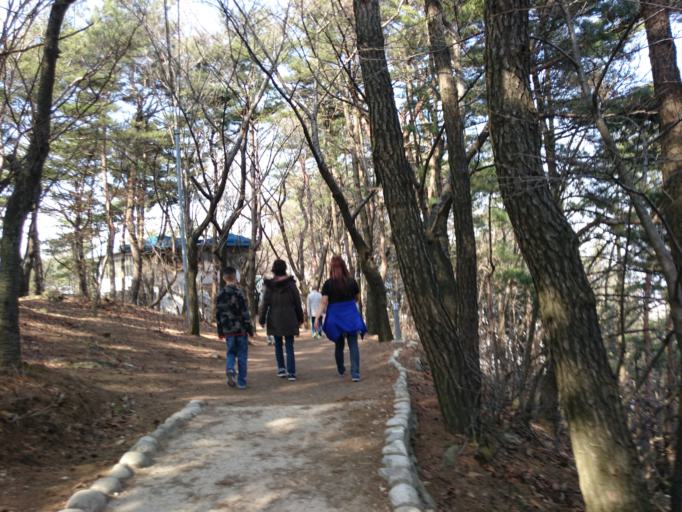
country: KR
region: Daegu
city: Daegu
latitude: 35.8236
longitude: 128.5793
